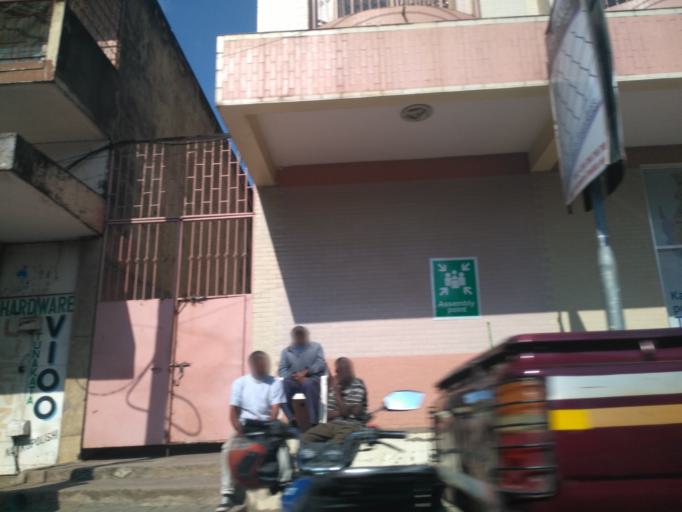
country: TZ
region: Arusha
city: Arusha
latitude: -3.3731
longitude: 36.6862
